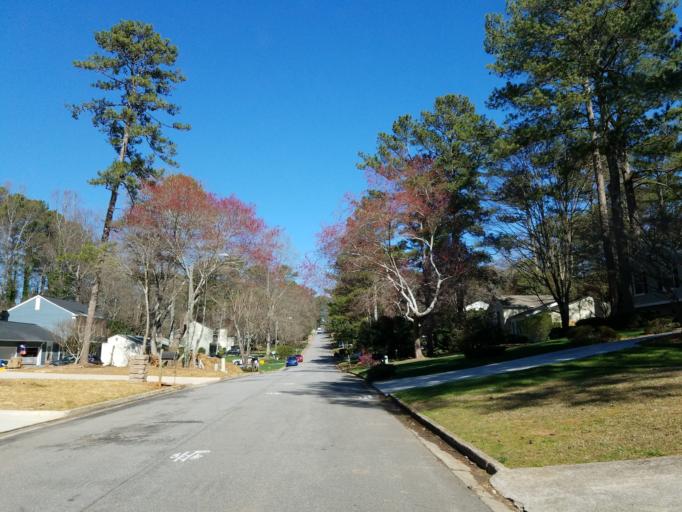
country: US
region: Georgia
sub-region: Cobb County
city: Marietta
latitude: 33.9611
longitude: -84.4683
